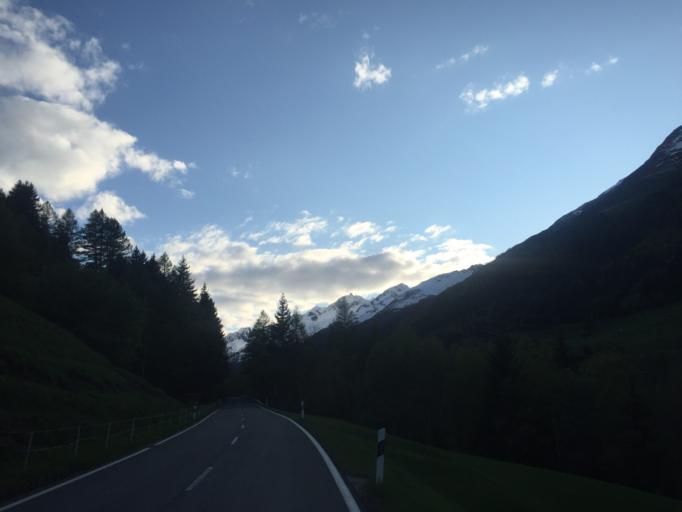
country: CH
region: Ticino
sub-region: Leventina District
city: Airolo
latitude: 46.5233
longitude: 8.5871
